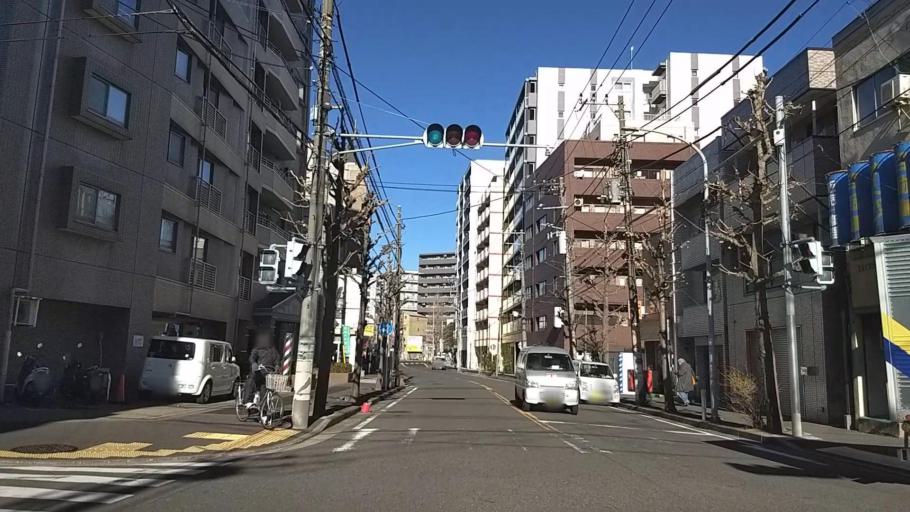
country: JP
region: Kanagawa
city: Yokohama
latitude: 35.4573
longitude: 139.6235
